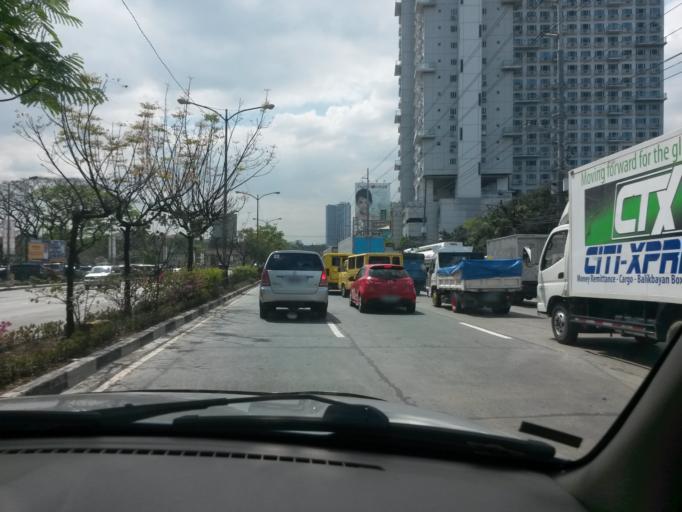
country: PH
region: Metro Manila
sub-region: Quezon City
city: Quezon City
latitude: 14.6459
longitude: 121.0744
